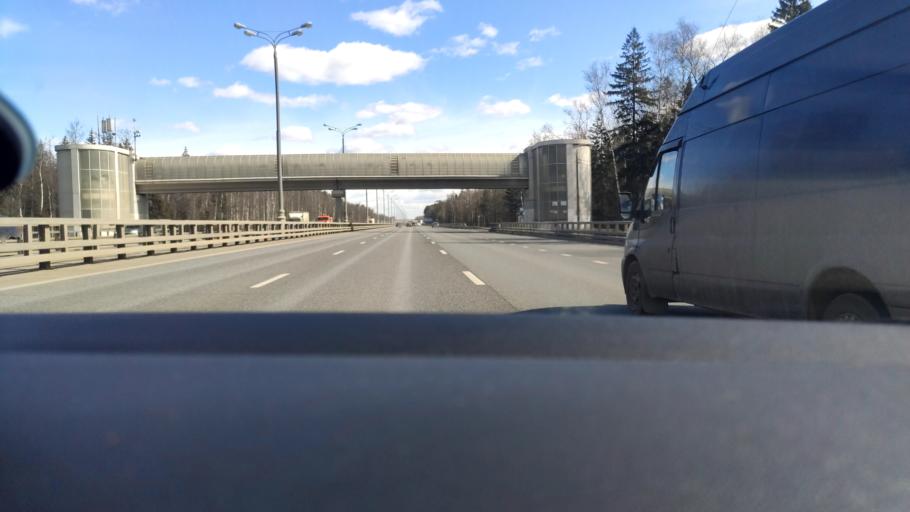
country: RU
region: Moskovskaya
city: Kokoshkino
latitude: 55.5592
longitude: 37.1609
